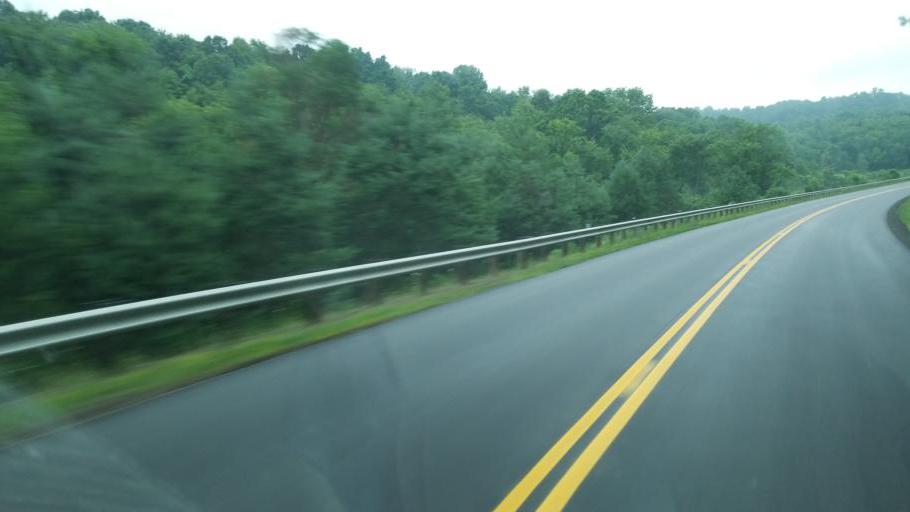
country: US
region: Ohio
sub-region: Tuscarawas County
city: Rockford
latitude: 40.4229
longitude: -81.2162
